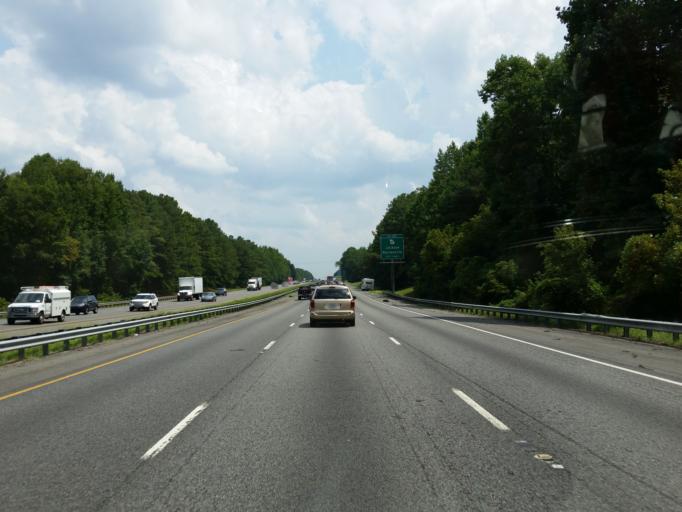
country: US
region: Georgia
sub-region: Henry County
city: Locust Grove
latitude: 33.2232
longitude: -84.0734
